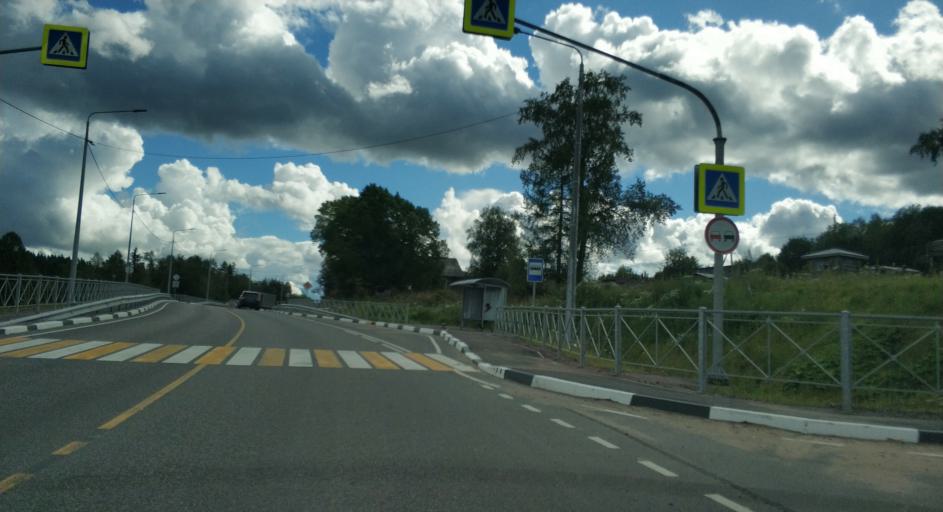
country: RU
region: Republic of Karelia
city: Ruskeala
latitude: 61.9344
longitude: 30.5912
